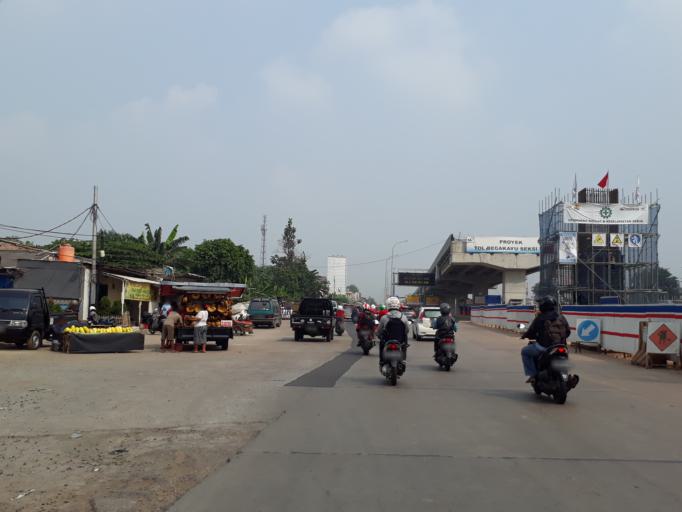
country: ID
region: West Java
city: Bekasi
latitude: -6.2497
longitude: 106.9656
